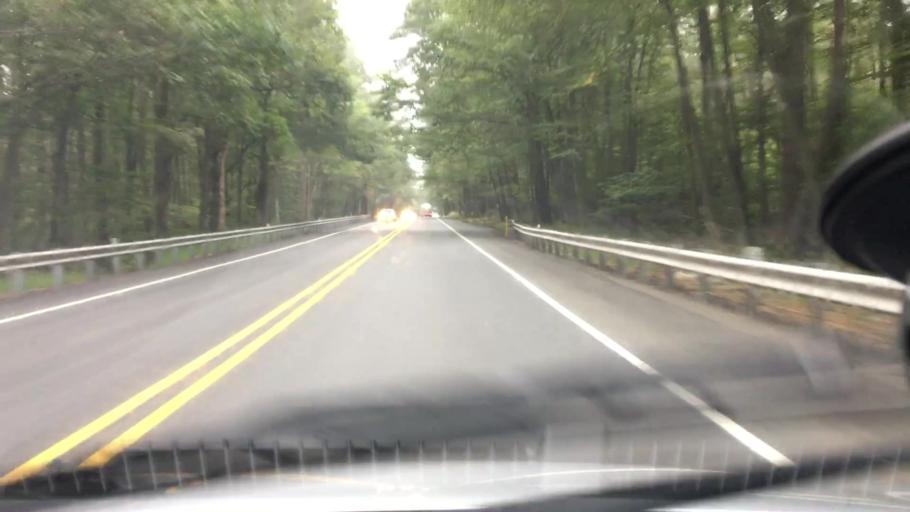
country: US
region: Pennsylvania
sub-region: Monroe County
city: Mount Pocono
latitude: 41.1291
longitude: -75.3344
